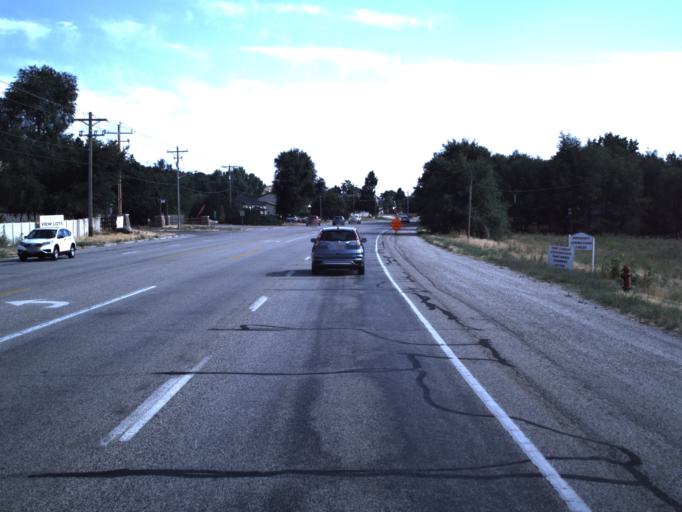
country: US
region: Utah
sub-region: Box Elder County
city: Willard
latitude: 41.3982
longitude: -112.0346
